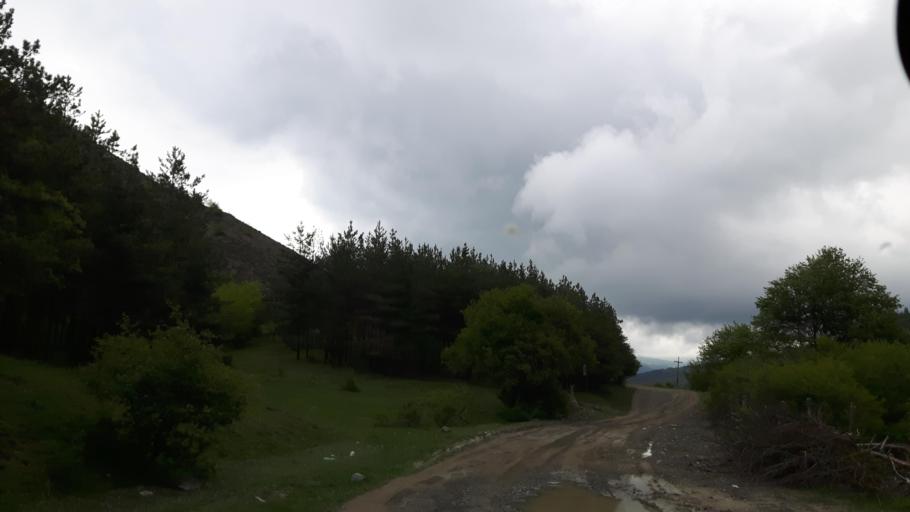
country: GE
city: Agara
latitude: 41.8643
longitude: 43.9184
